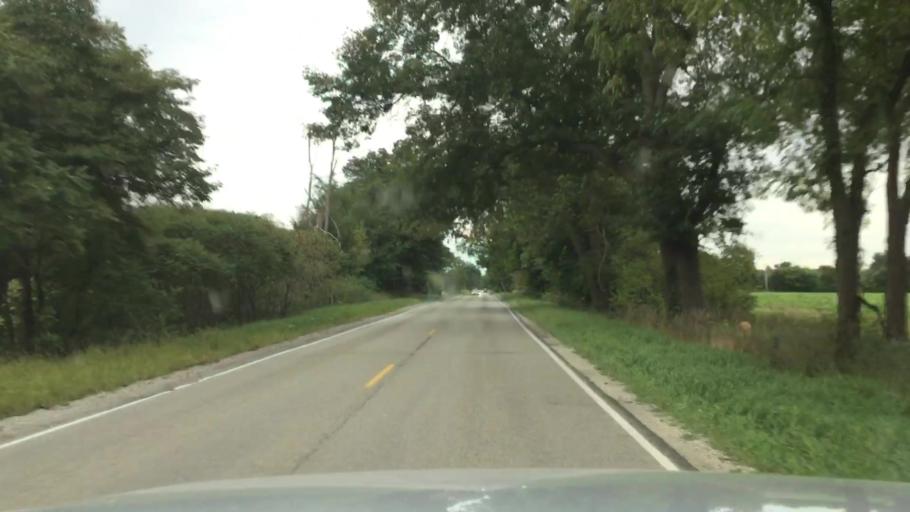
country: US
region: Michigan
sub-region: Genesee County
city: Argentine
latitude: 42.8056
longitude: -83.8785
